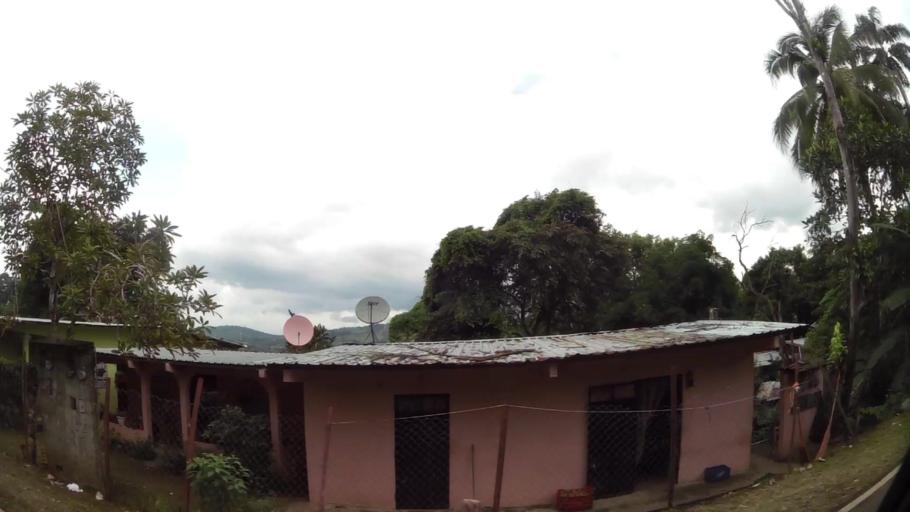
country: PA
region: Panama
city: Cabra Numero Uno
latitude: 9.1162
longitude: -79.3577
